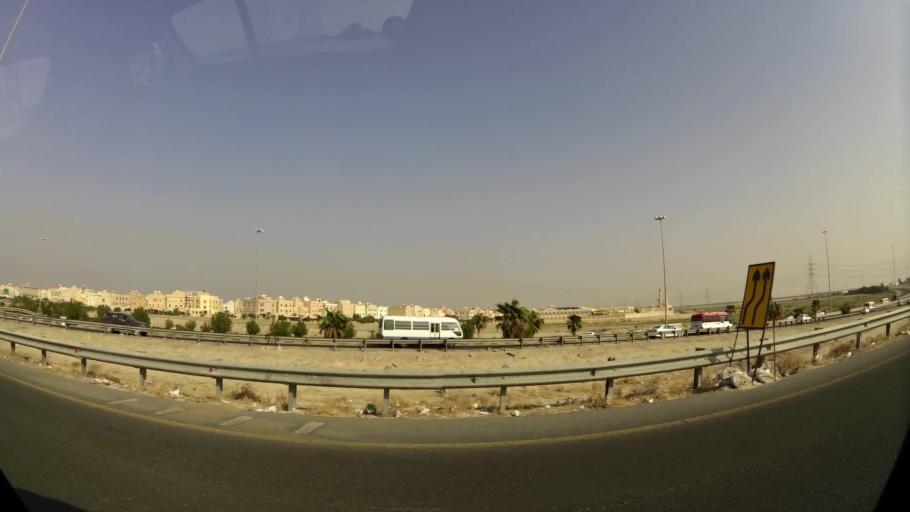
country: KW
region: Muhafazat al Jahra'
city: Al Jahra'
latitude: 29.3026
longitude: 47.7837
